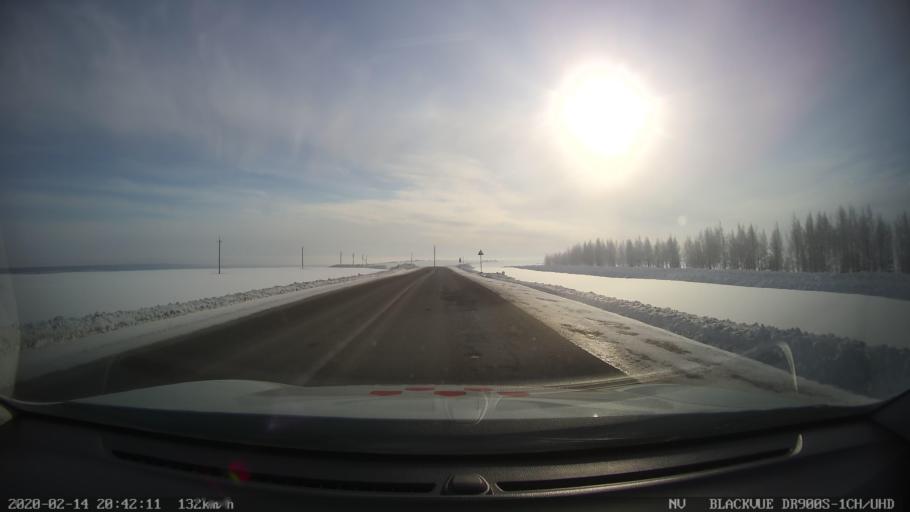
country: RU
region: Tatarstan
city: Kuybyshevskiy Zaton
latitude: 55.3198
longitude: 49.1381
